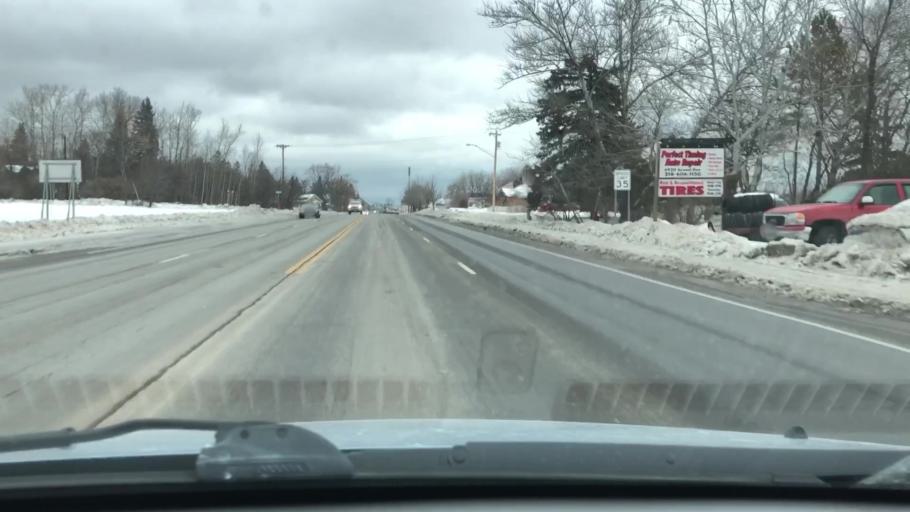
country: US
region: Minnesota
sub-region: Saint Louis County
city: Proctor
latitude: 46.7267
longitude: -92.1865
